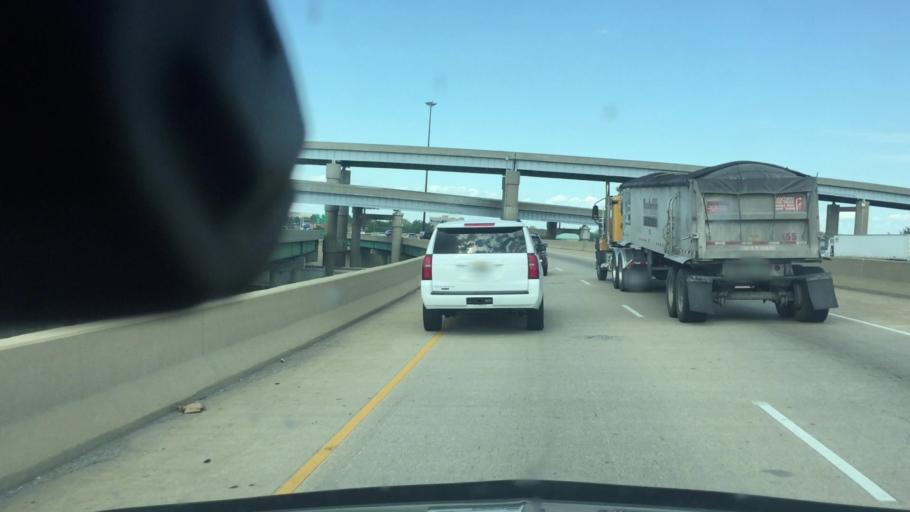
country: US
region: Illinois
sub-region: Saint Clair County
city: East Saint Louis
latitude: 38.6162
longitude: -90.1686
